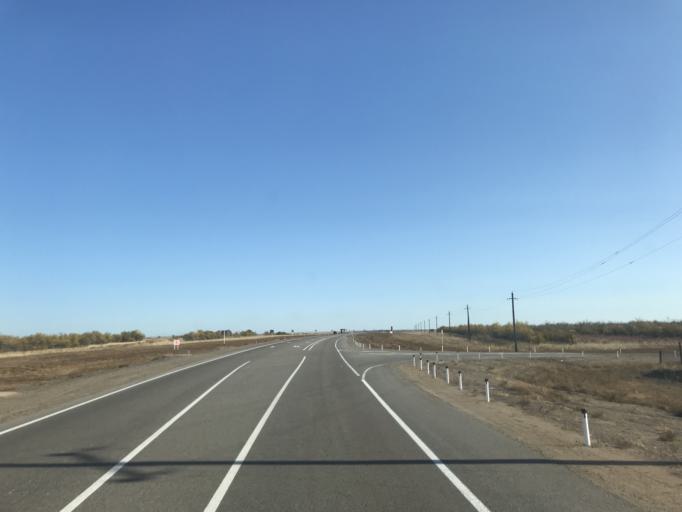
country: KZ
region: Pavlodar
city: Koktobe
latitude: 51.9016
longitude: 77.3840
